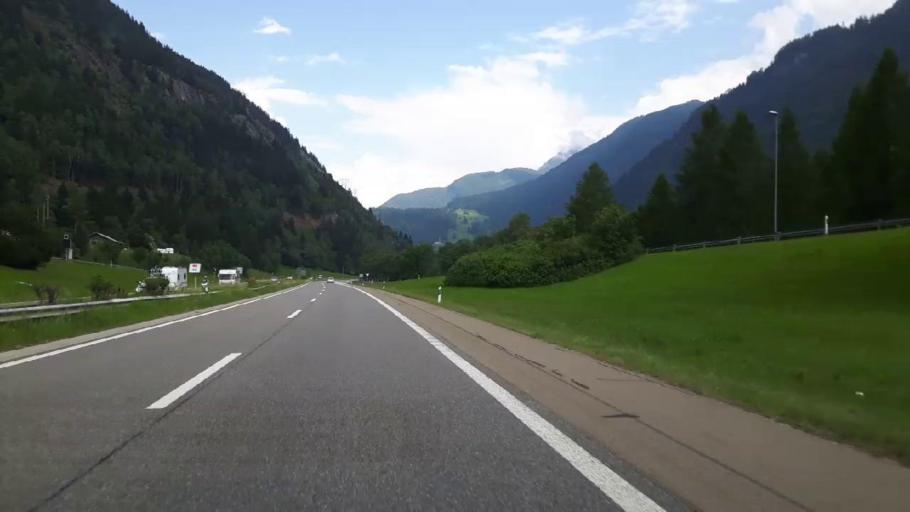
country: CH
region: Ticino
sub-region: Leventina District
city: Faido
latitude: 46.5003
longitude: 8.7269
